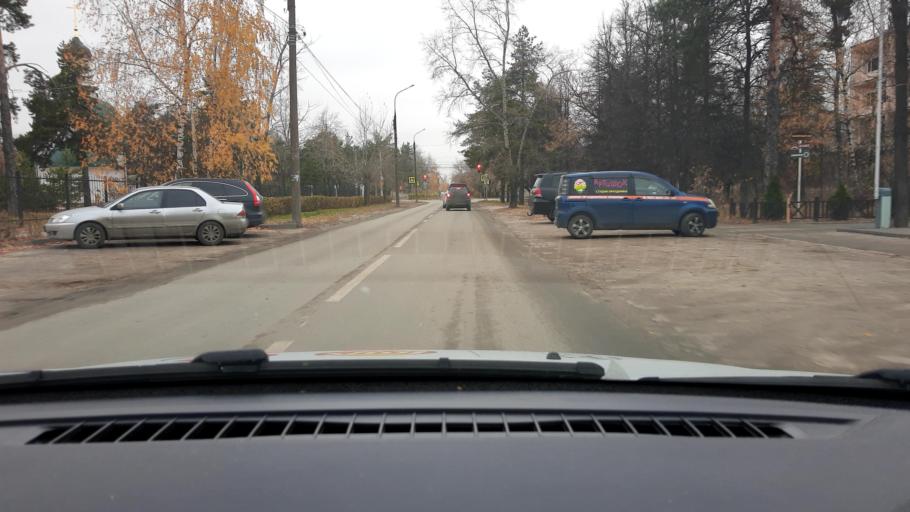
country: RU
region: Nizjnij Novgorod
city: Dzerzhinsk
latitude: 56.2470
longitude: 43.4464
